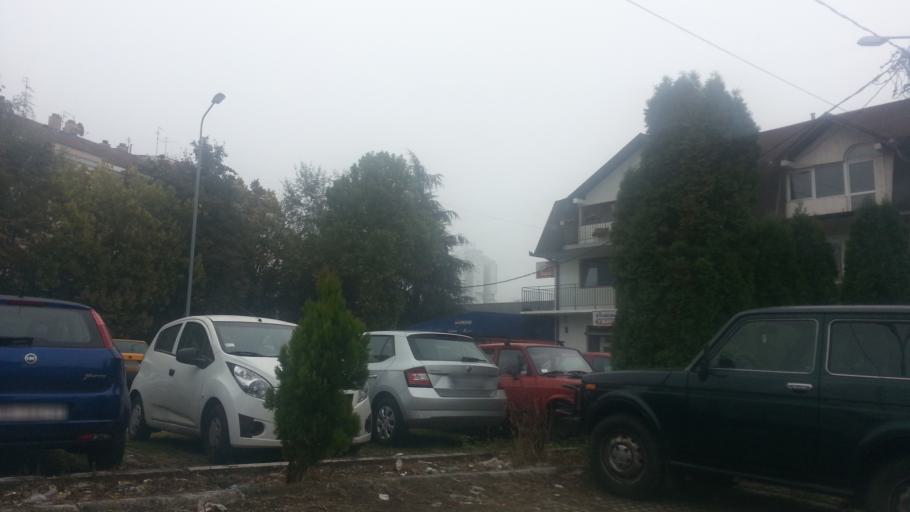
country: RS
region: Central Serbia
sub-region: Belgrade
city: Zemun
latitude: 44.8474
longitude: 20.3801
